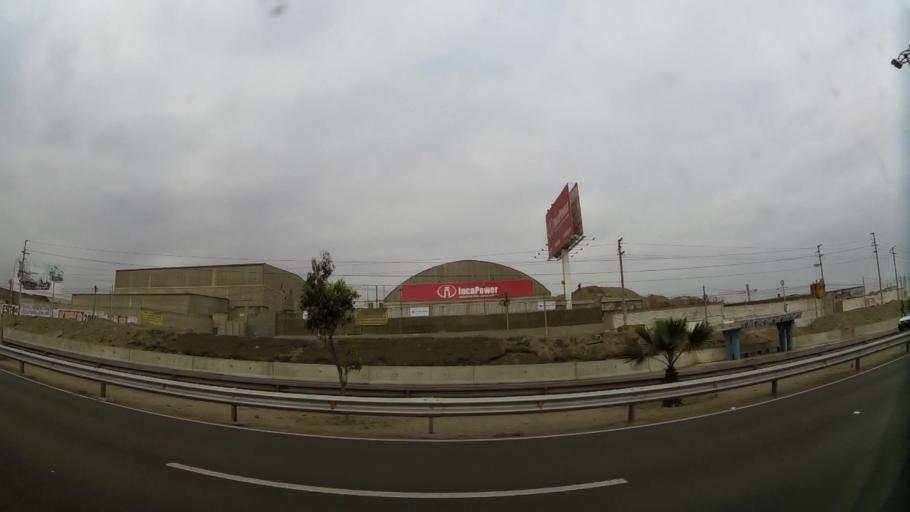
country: PE
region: Lima
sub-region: Lima
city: Surco
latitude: -12.2134
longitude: -76.9765
